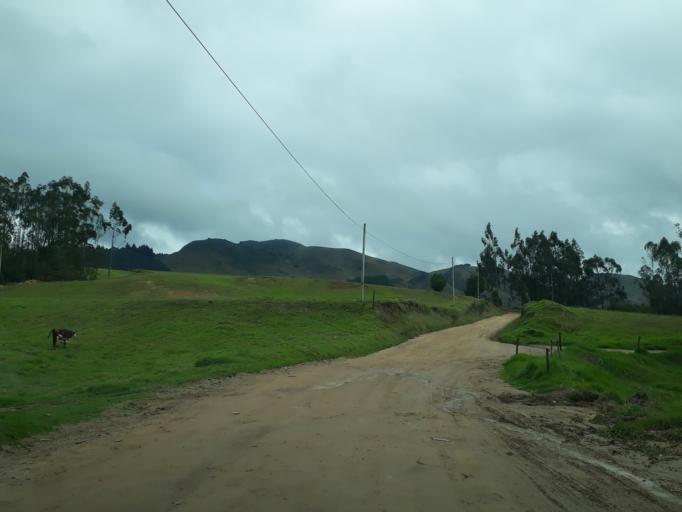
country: CO
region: Cundinamarca
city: Cucunuba
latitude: 5.1961
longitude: -73.7536
